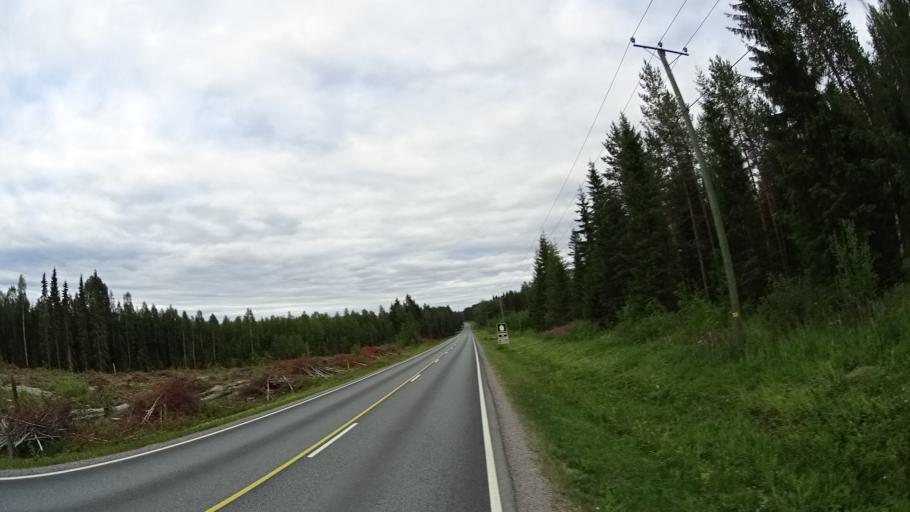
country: FI
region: Satakunta
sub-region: Pohjois-Satakunta
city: Jaemijaervi
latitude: 61.7772
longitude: 22.8684
